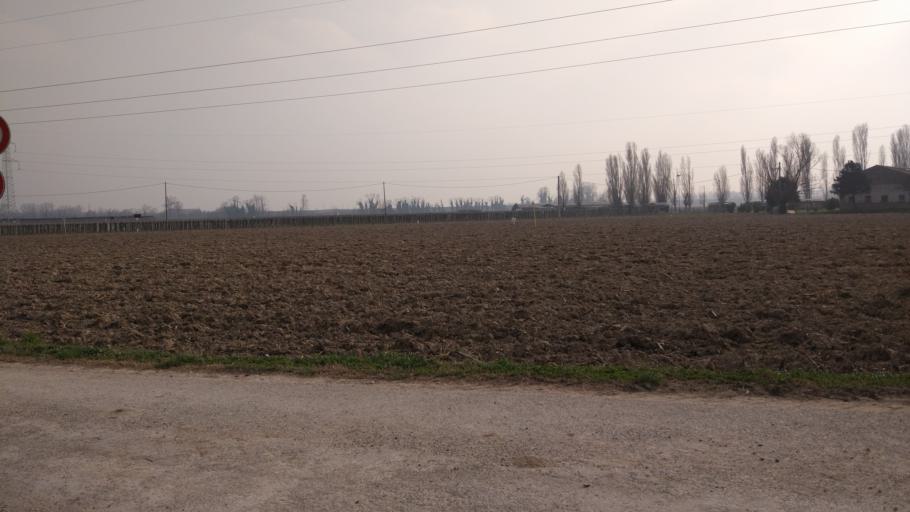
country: IT
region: Veneto
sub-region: Provincia di Verona
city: Caldierino-Rota
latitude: 45.3932
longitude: 11.1462
